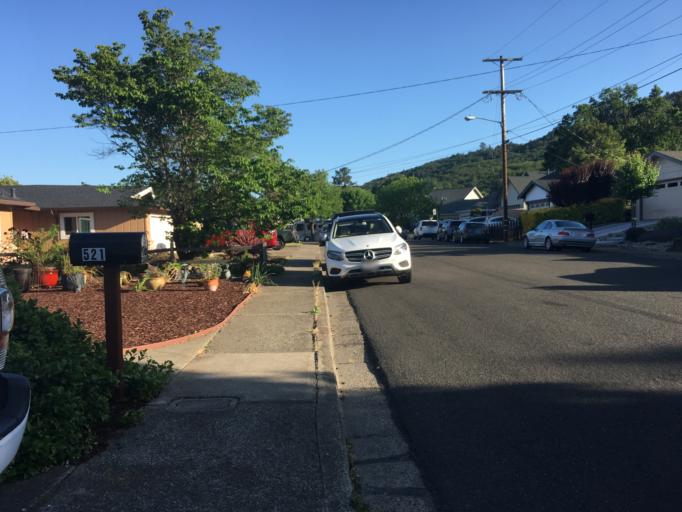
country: US
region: California
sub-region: Mendocino County
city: Ukiah
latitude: 39.1356
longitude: -123.2133
